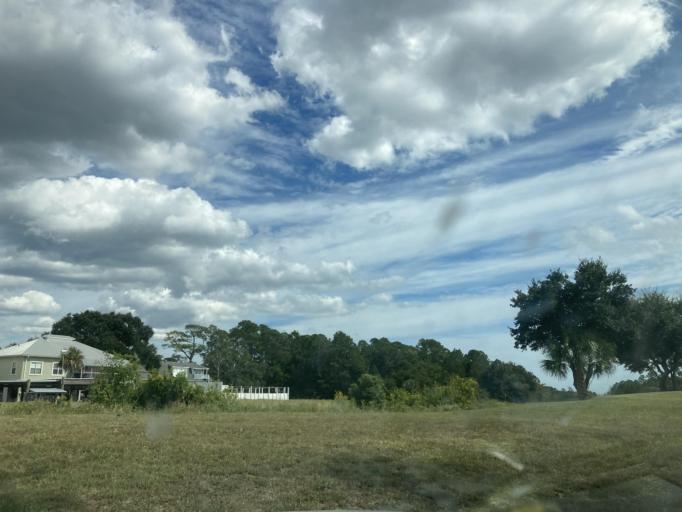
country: US
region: Mississippi
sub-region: Jackson County
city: Saint Martin
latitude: 30.4360
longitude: -88.8786
